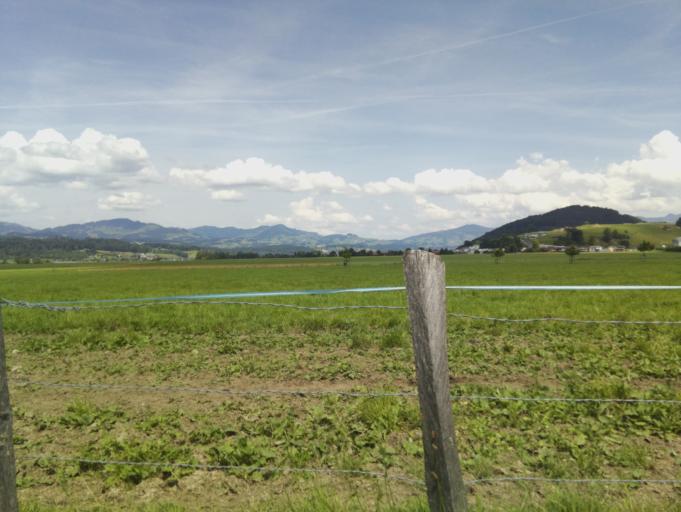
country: CH
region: Schwyz
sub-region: Bezirk March
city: Lachen
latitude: 47.1966
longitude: 8.8692
